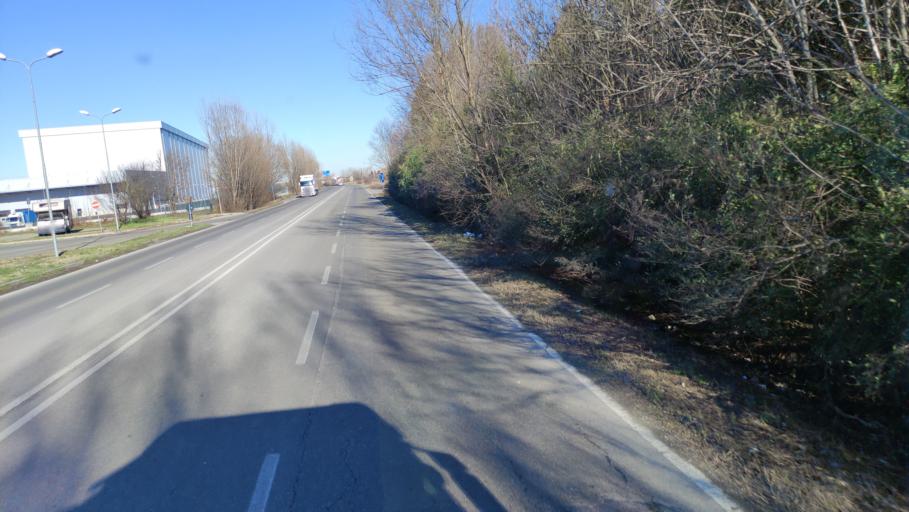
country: IT
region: Emilia-Romagna
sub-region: Provincia di Reggio Emilia
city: Correggio
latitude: 44.7618
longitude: 10.8093
